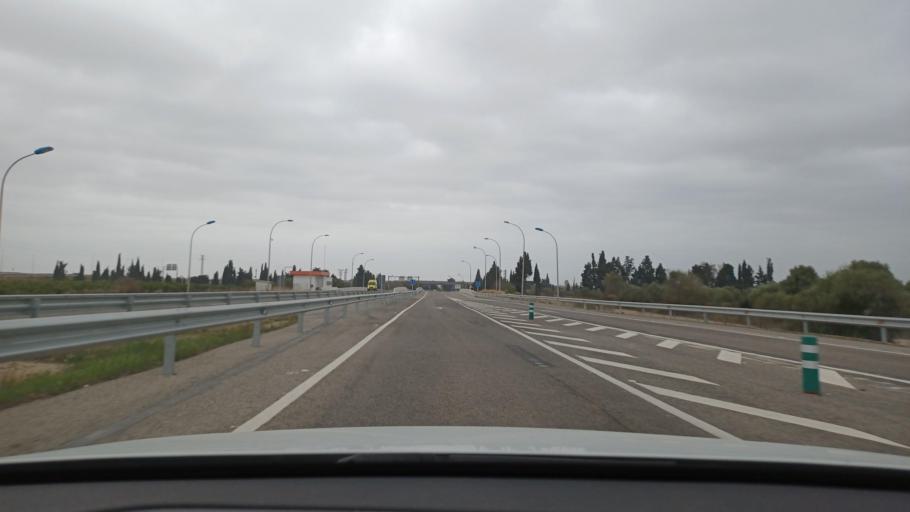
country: ES
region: Catalonia
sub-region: Provincia de Tarragona
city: Amposta
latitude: 40.7287
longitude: 0.5867
